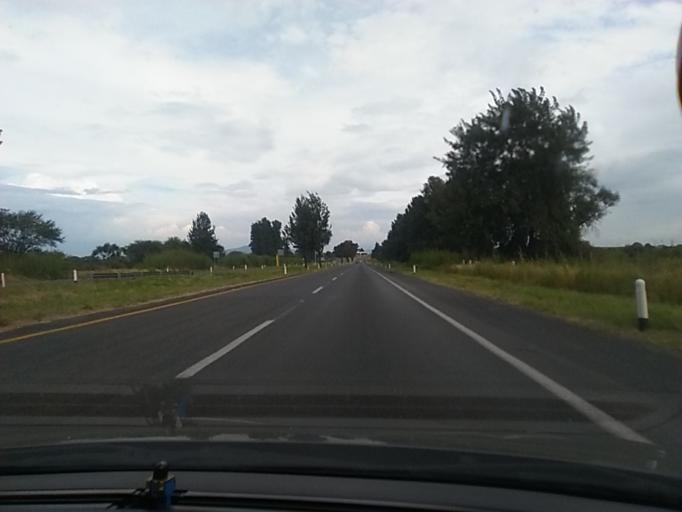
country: MX
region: Michoacan
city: Vistahermosa de Negrete
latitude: 20.2841
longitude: -102.4611
